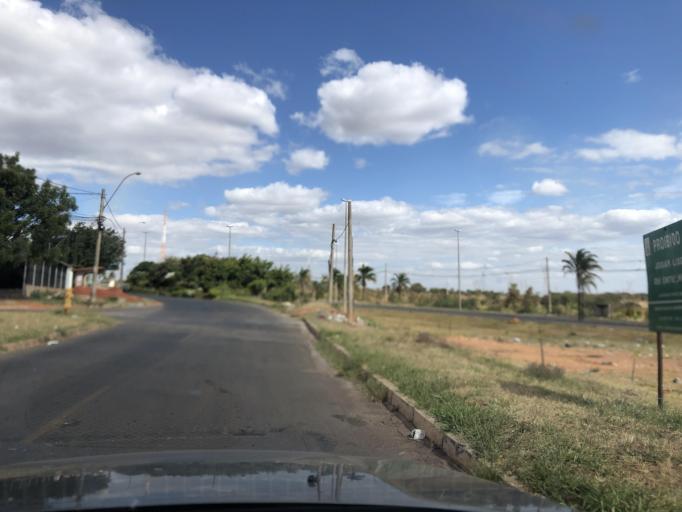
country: BR
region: Federal District
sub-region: Brasilia
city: Brasilia
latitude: -15.8857
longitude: -48.1300
